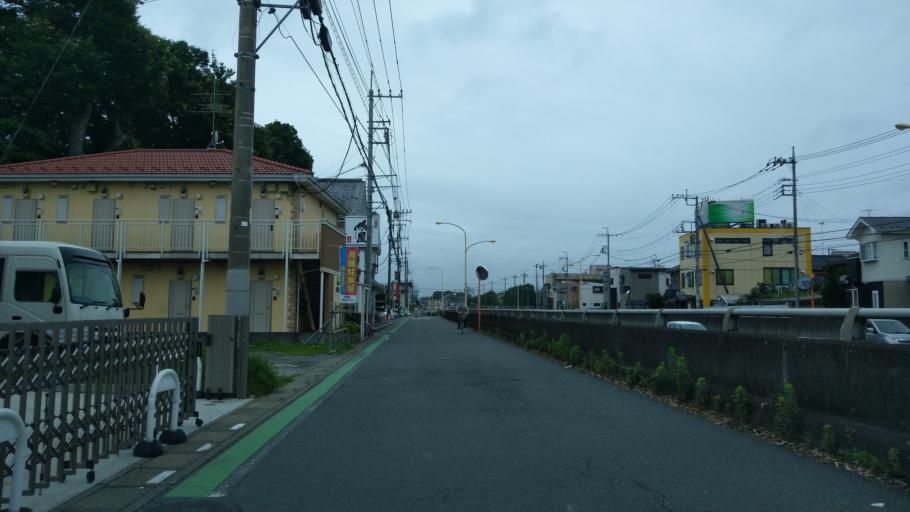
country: JP
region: Saitama
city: Saitama
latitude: 35.9301
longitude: 139.6461
